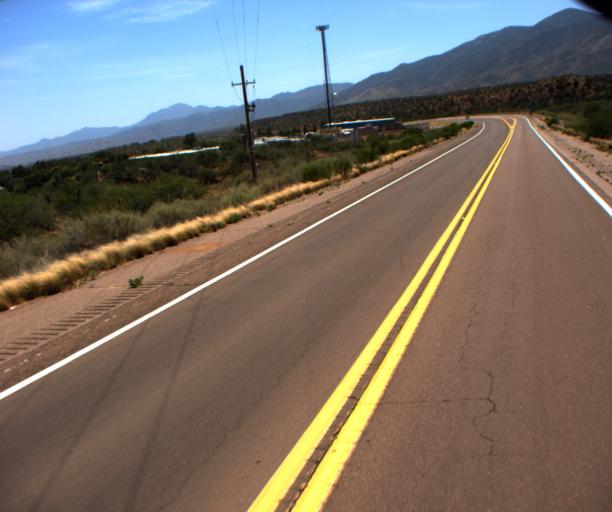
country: US
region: Arizona
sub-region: Gila County
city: Tonto Basin
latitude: 33.8802
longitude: -111.3137
